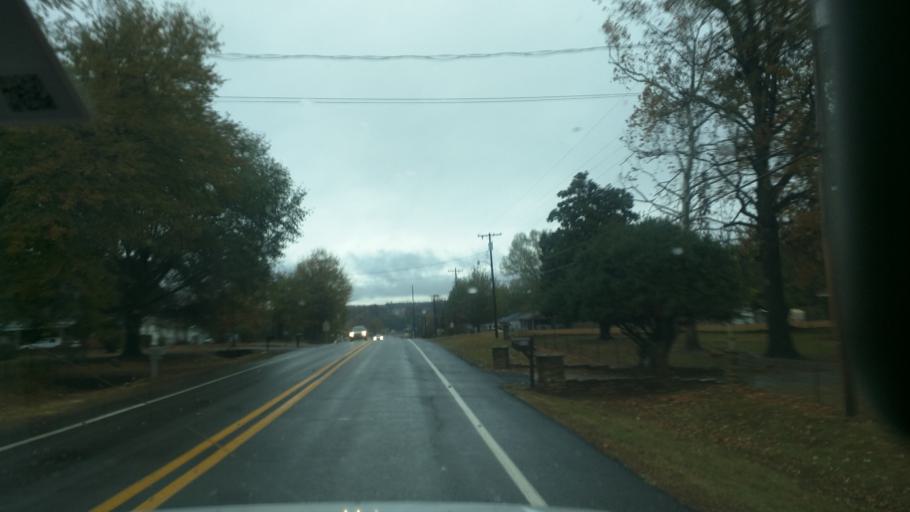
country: US
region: Arkansas
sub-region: Franklin County
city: Ozark
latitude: 35.4934
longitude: -93.8436
